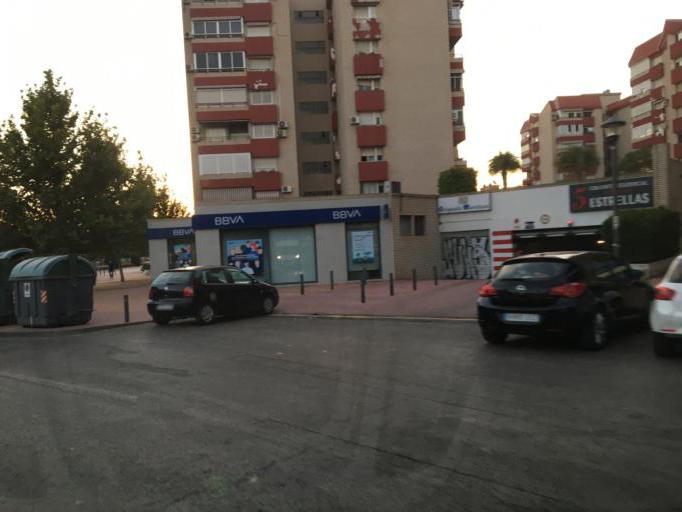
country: ES
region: Murcia
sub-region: Murcia
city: Murcia
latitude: 37.9809
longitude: -1.1213
